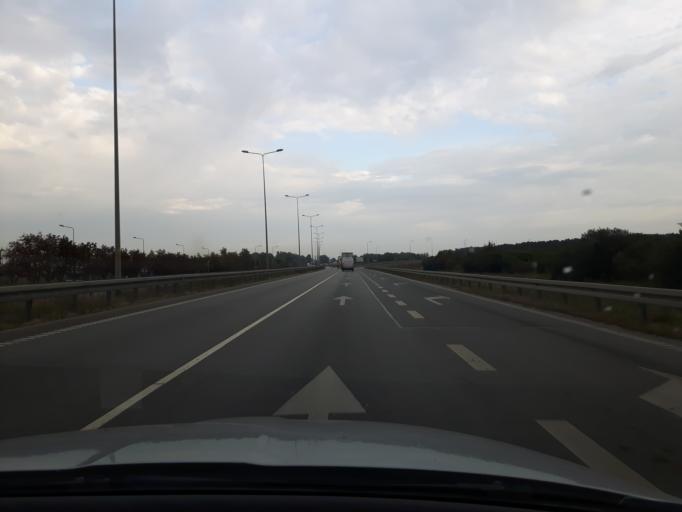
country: PL
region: Pomeranian Voivodeship
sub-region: Gdansk
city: Gdansk
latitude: 54.3634
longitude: 18.6901
